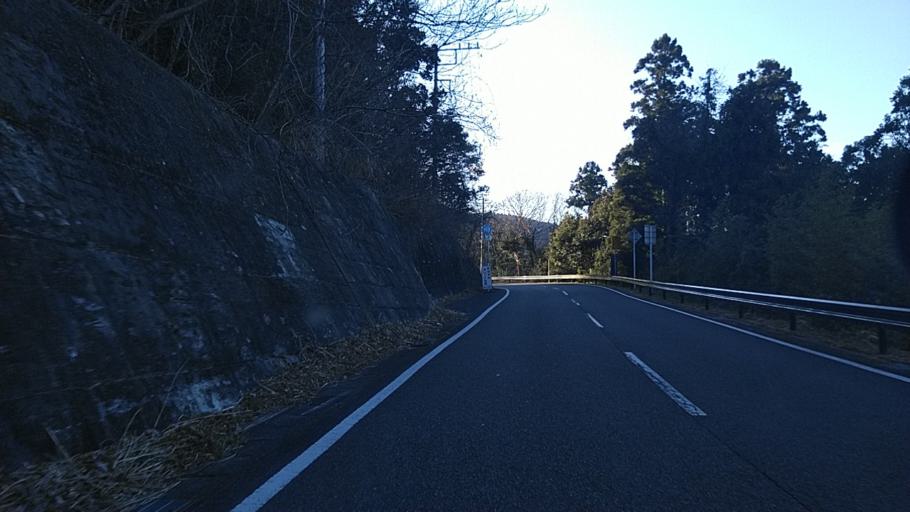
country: JP
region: Chiba
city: Kimitsu
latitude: 35.2594
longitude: 139.9340
